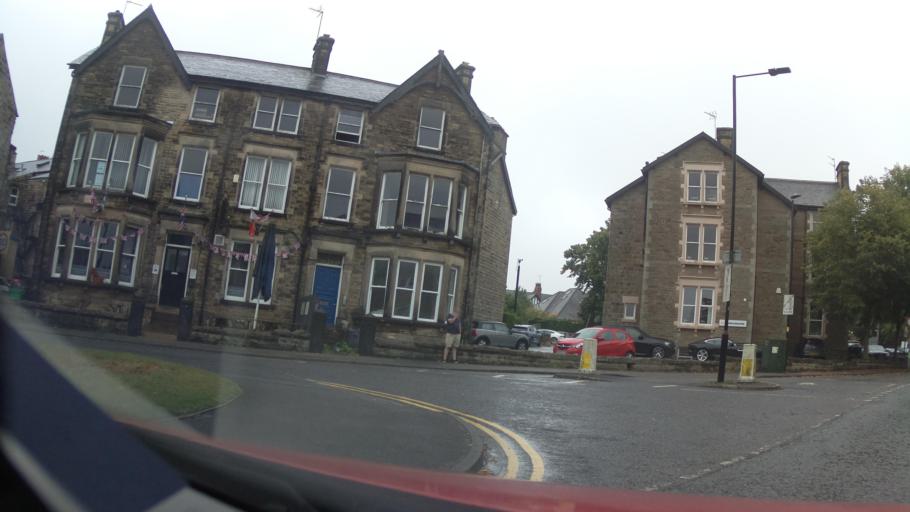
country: GB
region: England
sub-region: North Yorkshire
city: Harrogate
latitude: 53.9951
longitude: -1.5352
